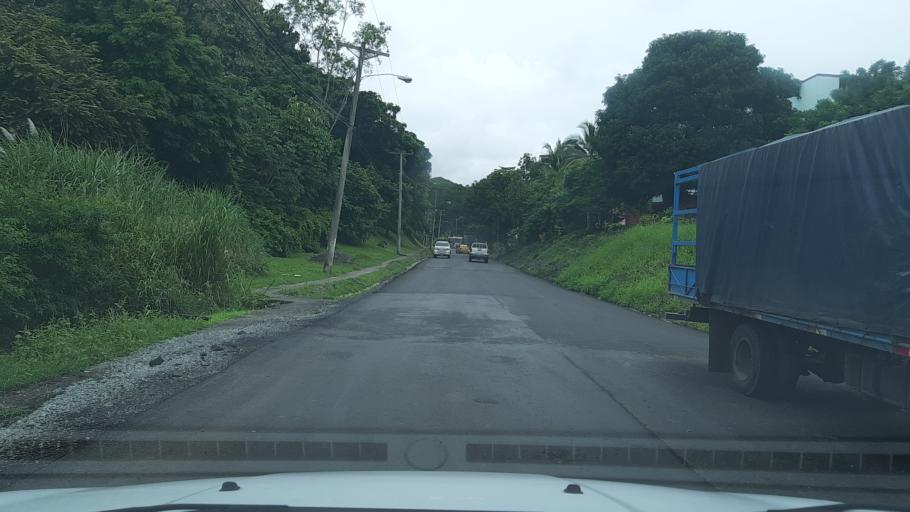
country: PA
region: Panama
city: San Miguelito
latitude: 9.0276
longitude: -79.4835
